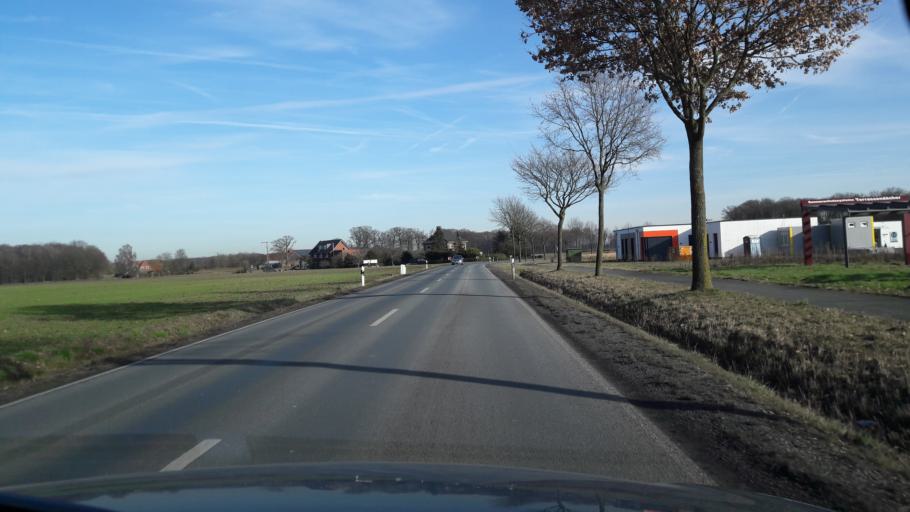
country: DE
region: North Rhine-Westphalia
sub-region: Regierungsbezirk Munster
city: Everswinkel
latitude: 51.9341
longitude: 7.8565
